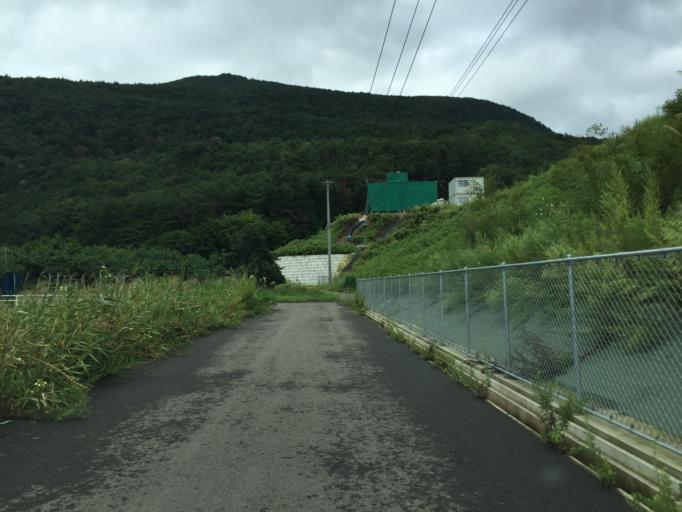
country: JP
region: Fukushima
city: Fukushima-shi
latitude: 37.8073
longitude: 140.4070
